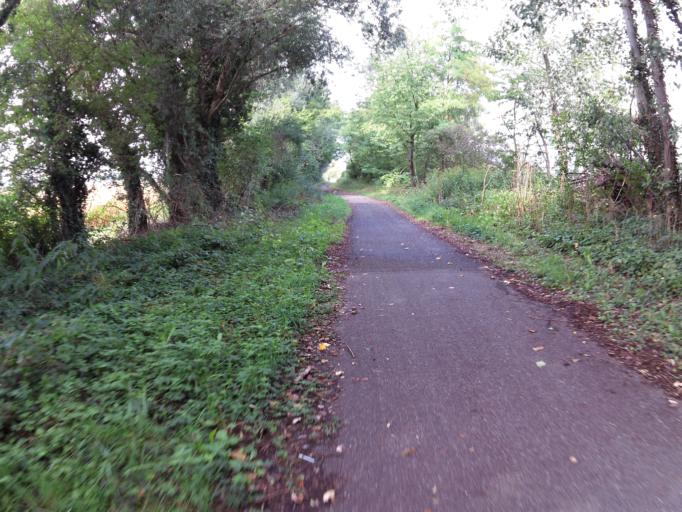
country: FR
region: Alsace
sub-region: Departement du Haut-Rhin
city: Kunheim
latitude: 48.0630
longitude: 7.5436
